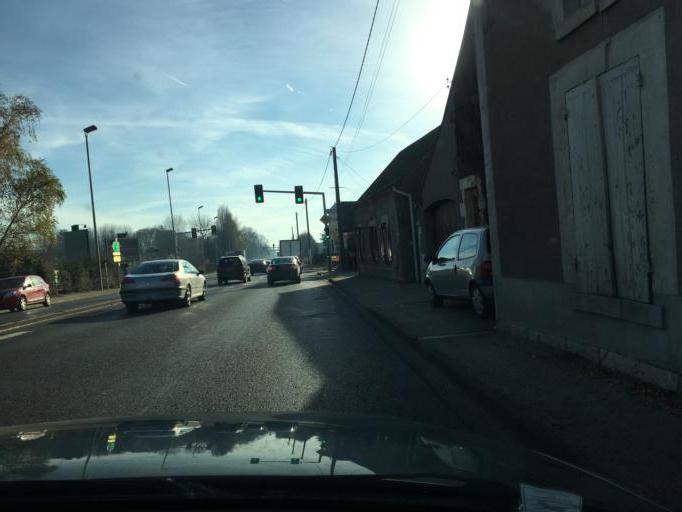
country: FR
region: Centre
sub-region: Departement du Loiret
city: Saran
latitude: 47.9524
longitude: 1.8915
